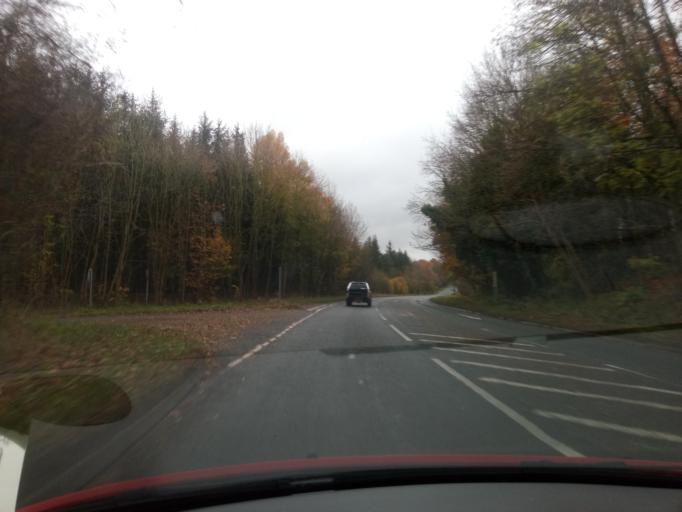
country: GB
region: England
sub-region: County Durham
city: High Etherley
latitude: 54.6679
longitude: -1.7737
